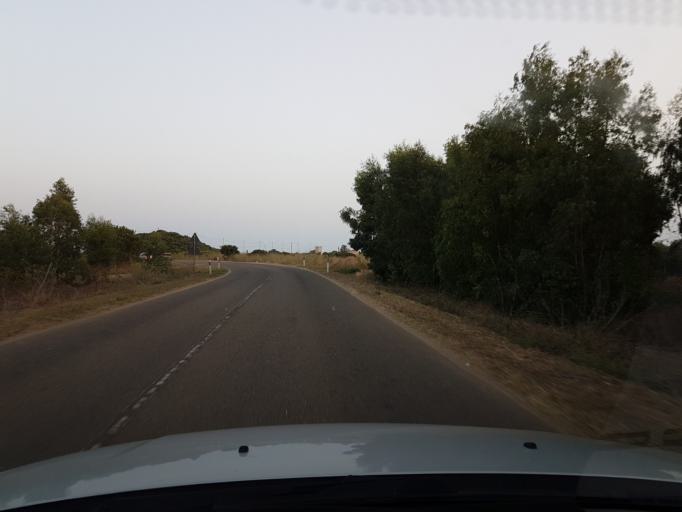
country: IT
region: Sardinia
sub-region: Provincia di Oristano
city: Cabras
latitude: 39.9186
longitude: 8.4512
